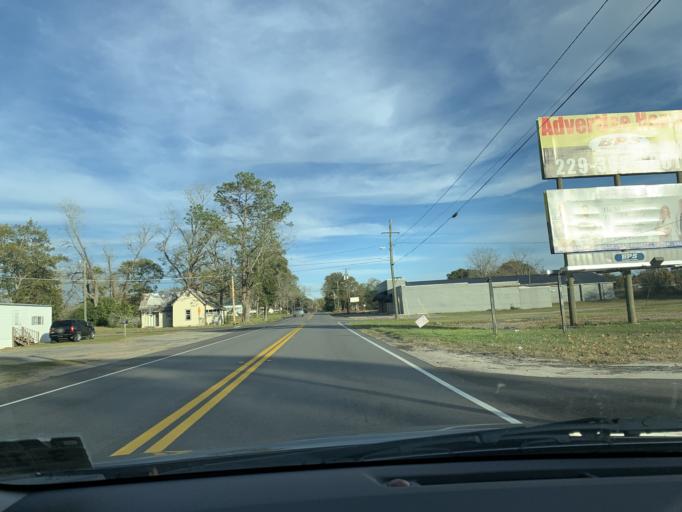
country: US
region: Georgia
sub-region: Irwin County
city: Ocilla
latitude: 31.5941
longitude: -83.2455
